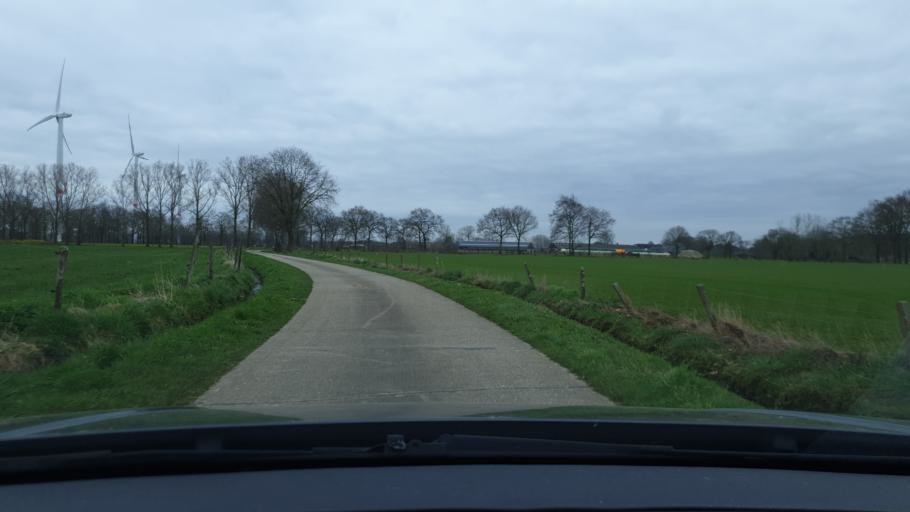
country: BE
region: Flanders
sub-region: Provincie Antwerpen
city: Westerlo
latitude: 51.1275
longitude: 4.9192
